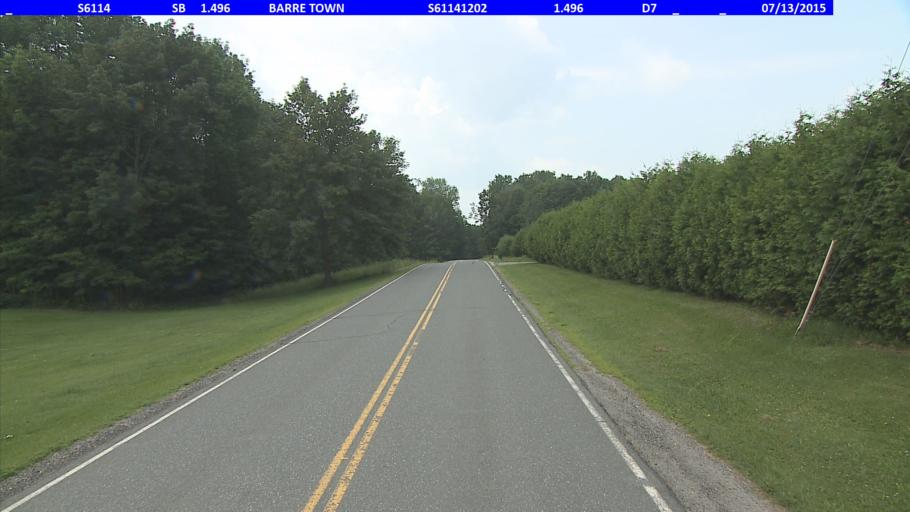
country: US
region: Vermont
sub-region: Washington County
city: Barre
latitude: 44.2097
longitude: -72.4681
